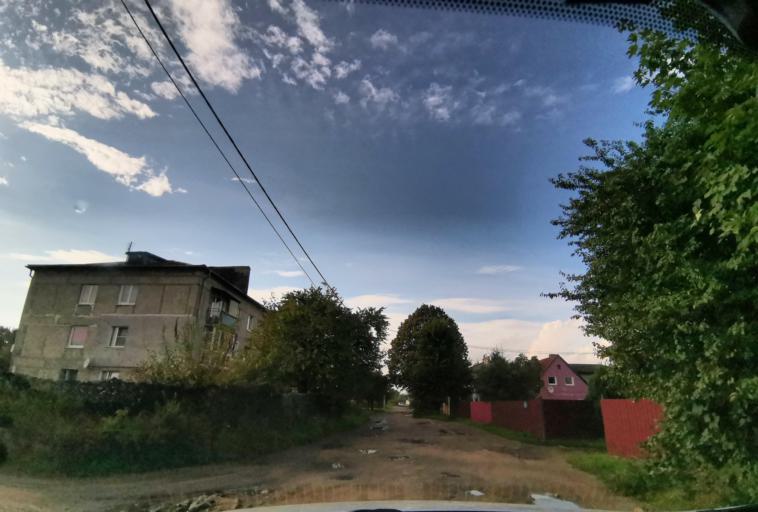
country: RU
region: Kaliningrad
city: Chernyakhovsk
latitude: 54.6569
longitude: 21.8367
